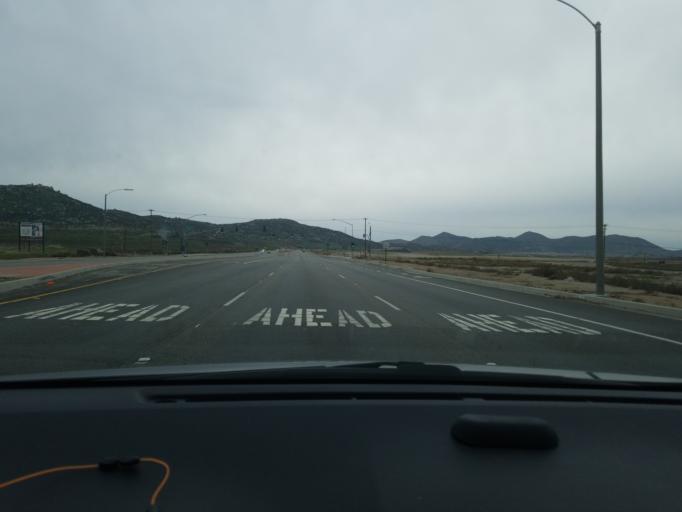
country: US
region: California
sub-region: Riverside County
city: Winchester
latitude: 33.6925
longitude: -117.1178
